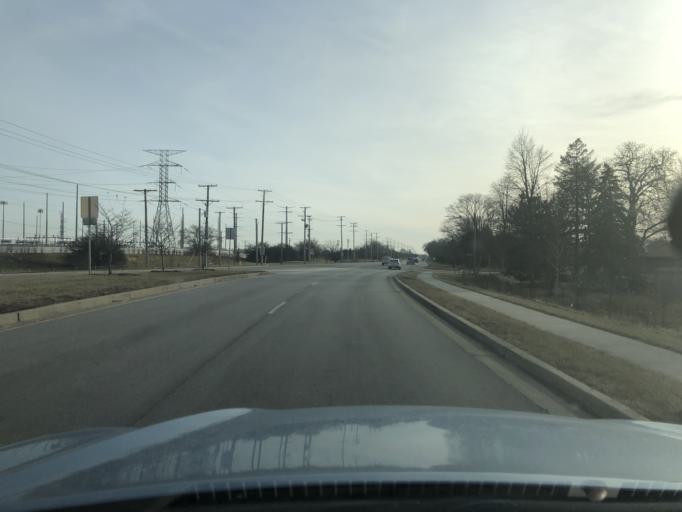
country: US
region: Illinois
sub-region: DuPage County
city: Itasca
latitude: 41.9816
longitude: -87.9983
